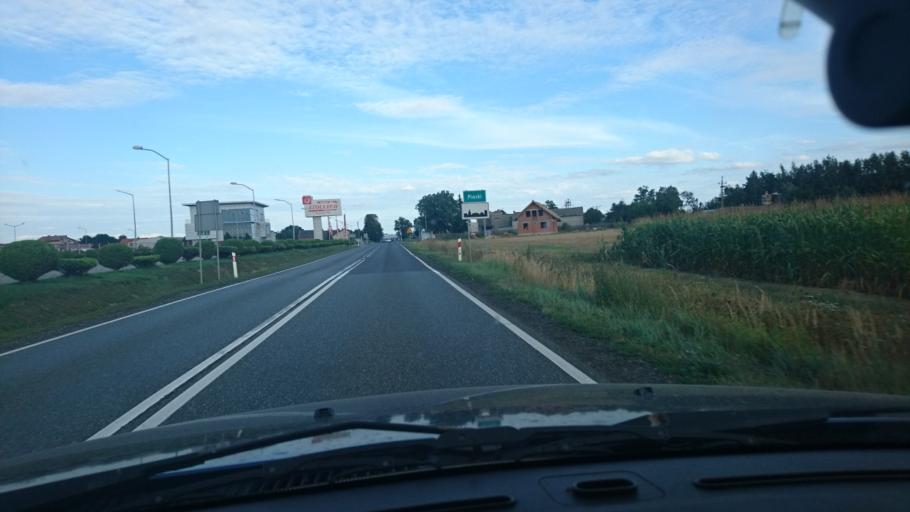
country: PL
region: Greater Poland Voivodeship
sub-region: Powiat kepinski
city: Slupia pod Kepnem
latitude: 51.2312
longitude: 18.0716
